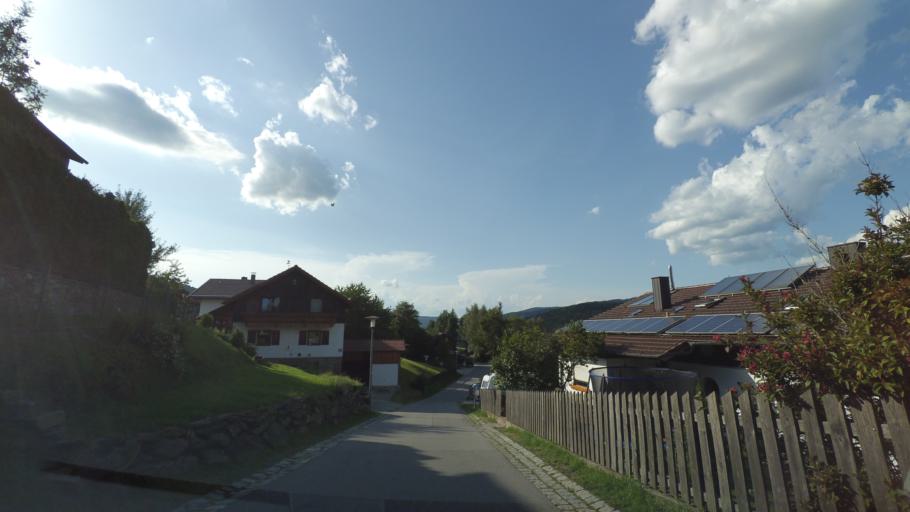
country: DE
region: Bavaria
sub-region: Upper Palatinate
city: Lohberg
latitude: 49.1729
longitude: 13.0778
